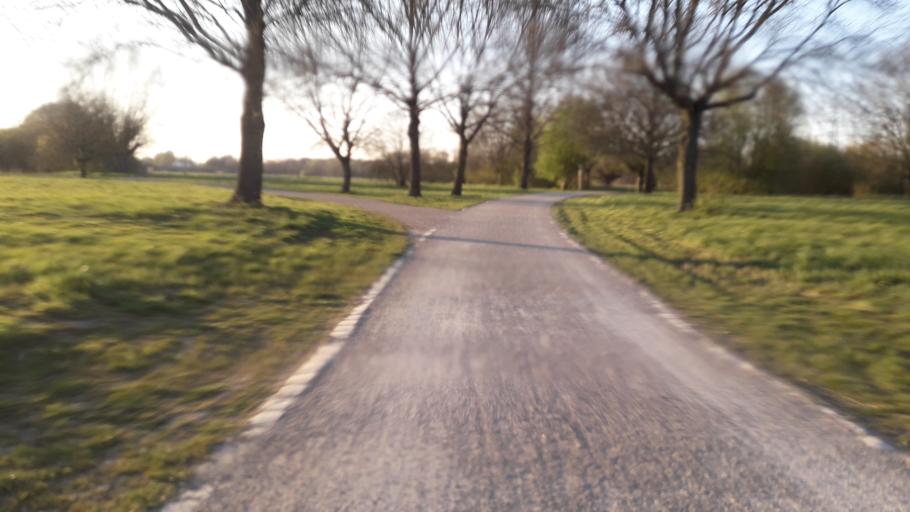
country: DE
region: North Rhine-Westphalia
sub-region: Regierungsbezirk Detmold
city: Paderborn
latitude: 51.7496
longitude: 8.7030
